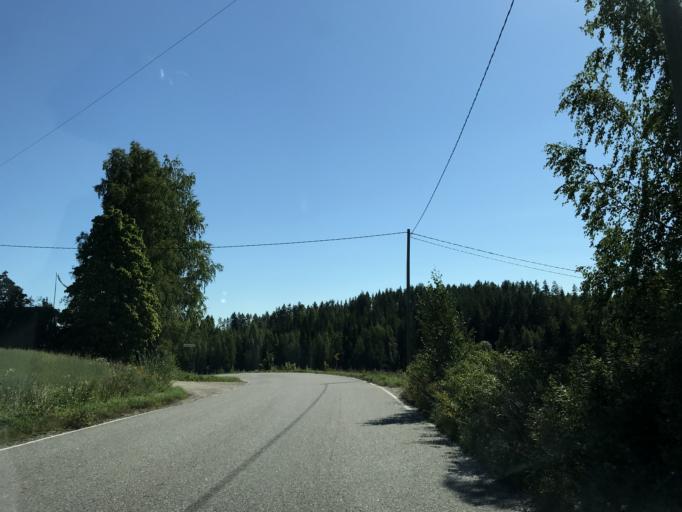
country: FI
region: Paijanne Tavastia
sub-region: Lahti
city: Orimattila
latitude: 60.8074
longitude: 25.6855
